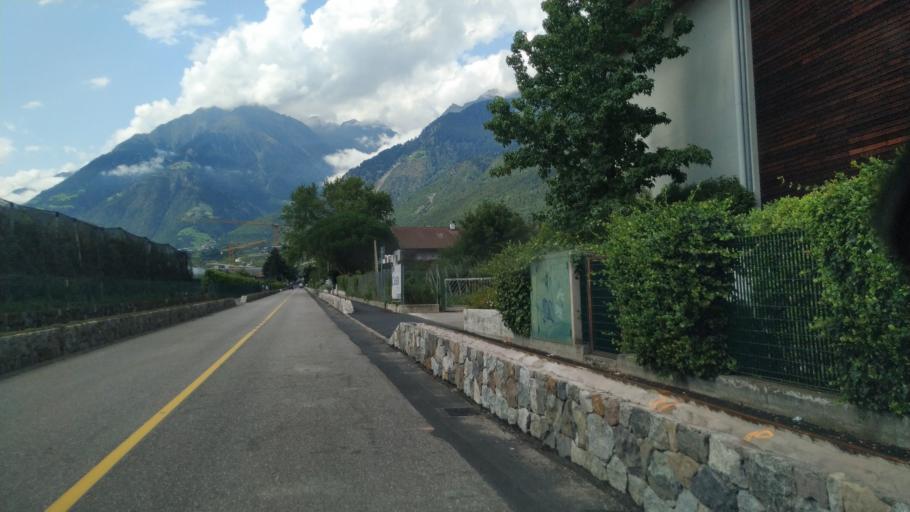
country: IT
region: Trentino-Alto Adige
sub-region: Bolzano
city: Lagundo
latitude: 46.6785
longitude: 11.1423
